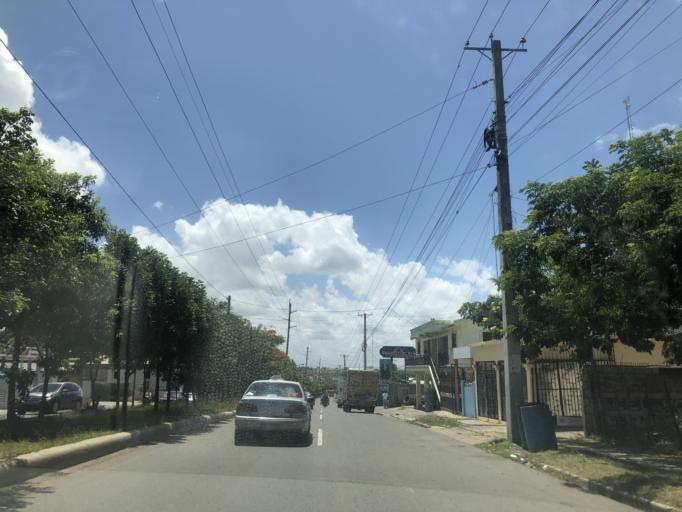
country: DO
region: Santiago
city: Santiago de los Caballeros
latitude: 19.4408
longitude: -70.7304
